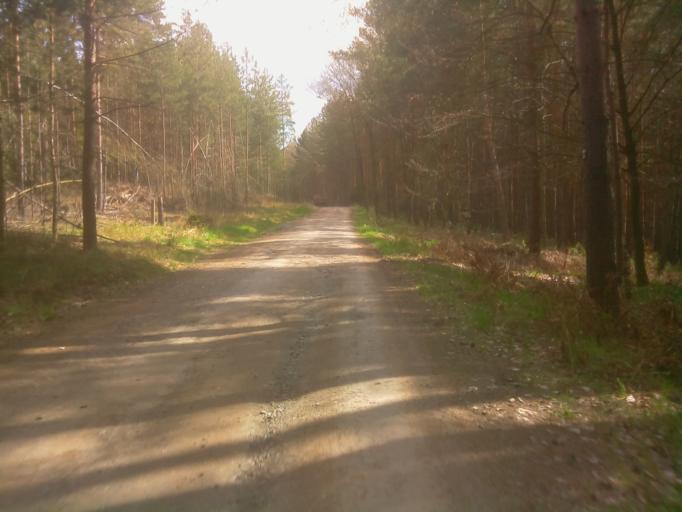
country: DE
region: Thuringia
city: Bremsnitz
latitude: 50.7907
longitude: 11.7566
